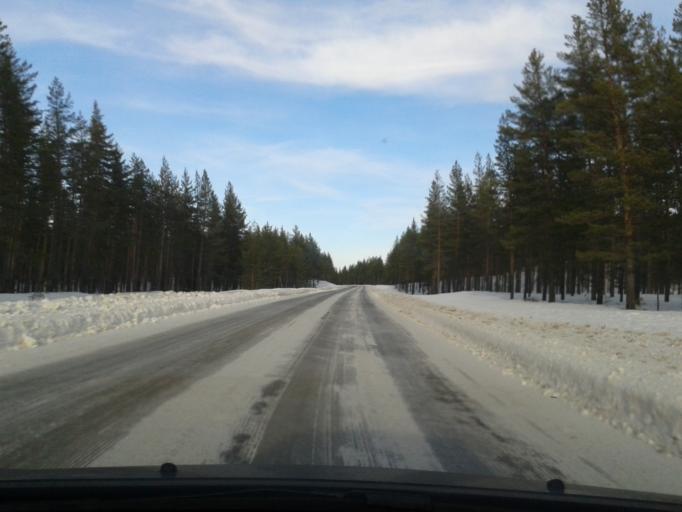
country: SE
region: Vaesternorrland
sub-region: OErnskoeldsviks Kommun
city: Bredbyn
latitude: 63.6125
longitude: 17.9027
